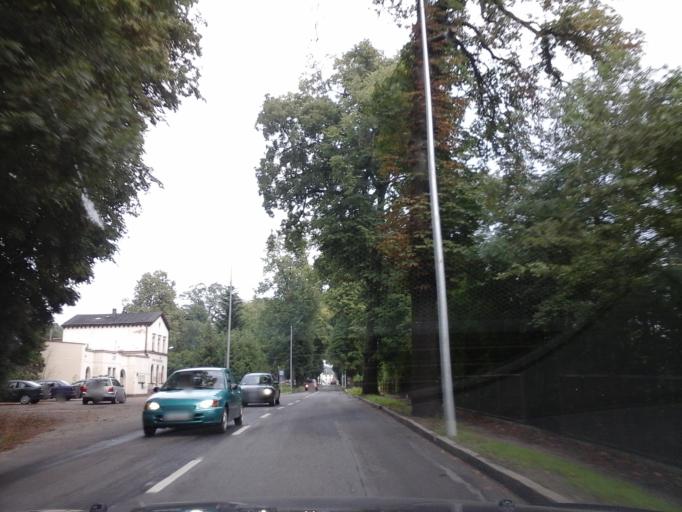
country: PL
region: Lubusz
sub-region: Powiat strzelecko-drezdenecki
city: Drezdenko
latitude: 52.8534
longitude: 15.8327
